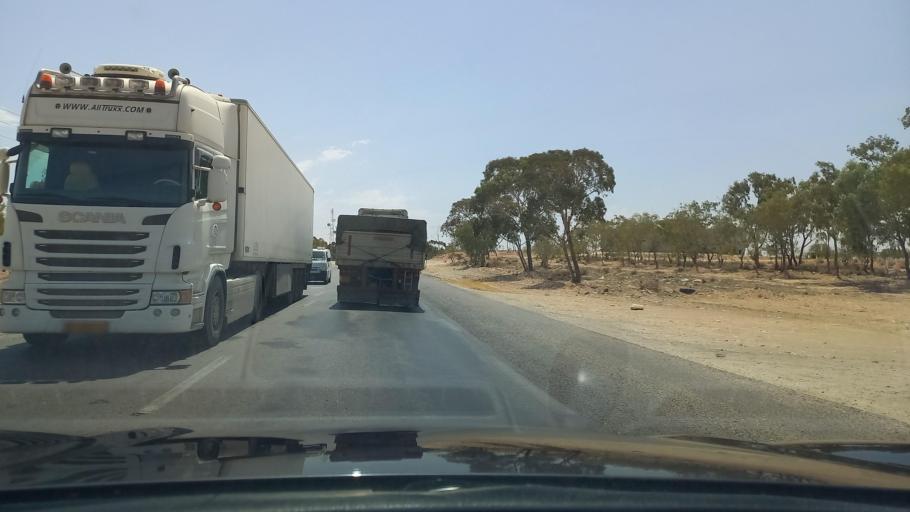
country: TN
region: Madanin
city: Medenine
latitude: 33.5736
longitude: 10.3169
